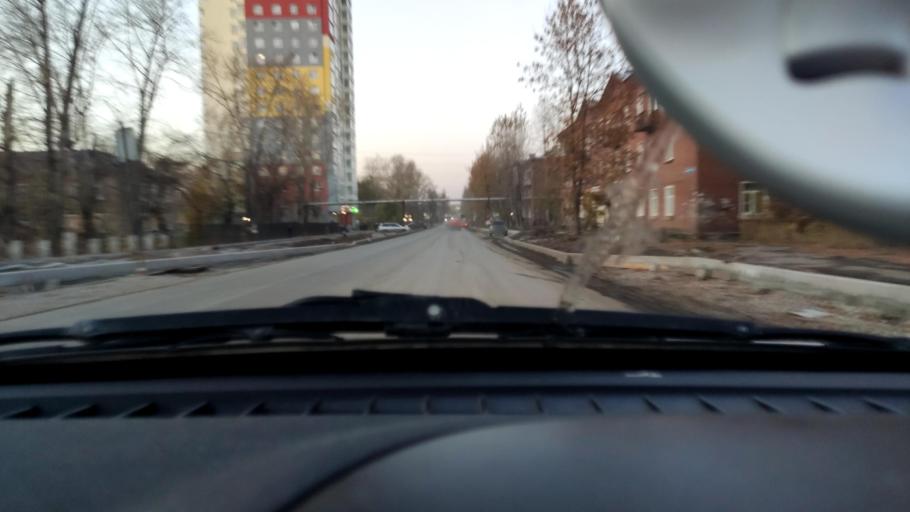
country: RU
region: Perm
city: Perm
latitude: 57.9696
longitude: 56.2741
